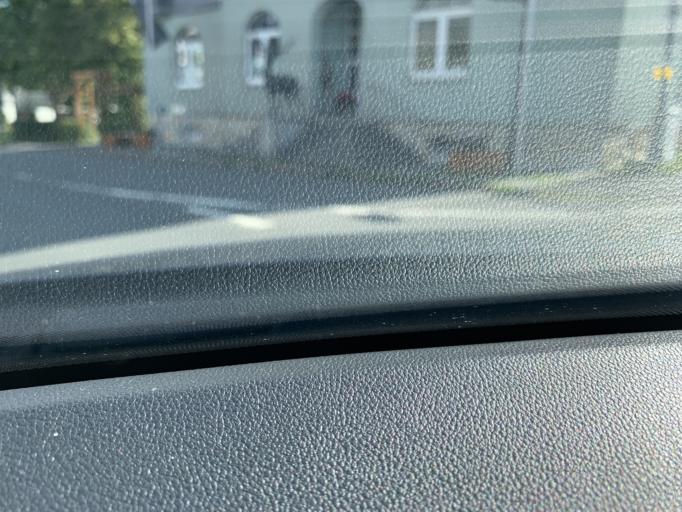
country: DE
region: Thuringia
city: Neuhaus am Rennweg
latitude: 50.5023
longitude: 11.1485
